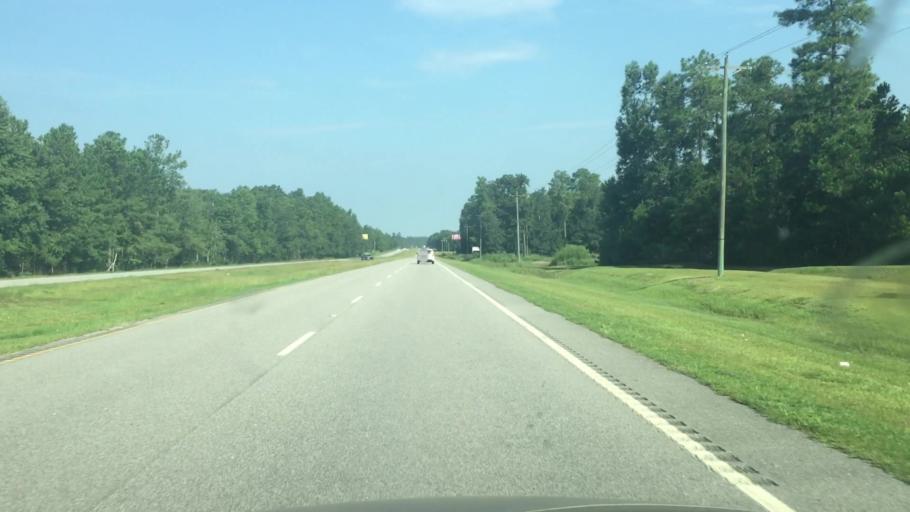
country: US
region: South Carolina
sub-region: Horry County
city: Loris
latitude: 34.0550
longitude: -78.8419
